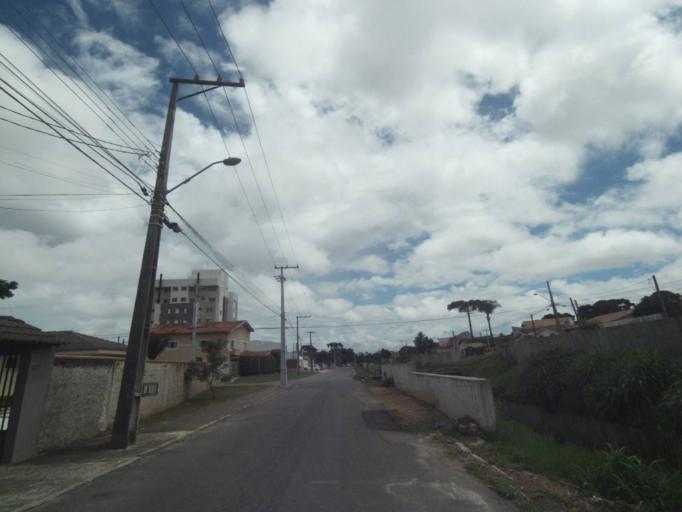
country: BR
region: Parana
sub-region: Curitiba
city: Curitiba
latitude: -25.4839
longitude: -49.2772
